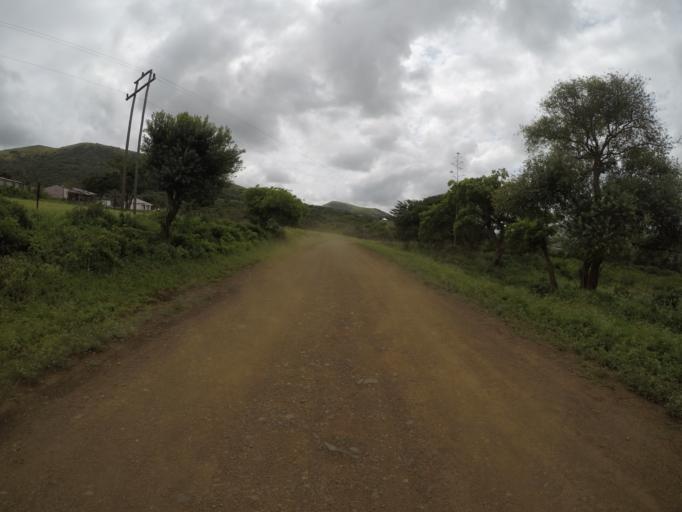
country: ZA
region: KwaZulu-Natal
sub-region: uThungulu District Municipality
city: Empangeni
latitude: -28.5923
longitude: 31.8829
